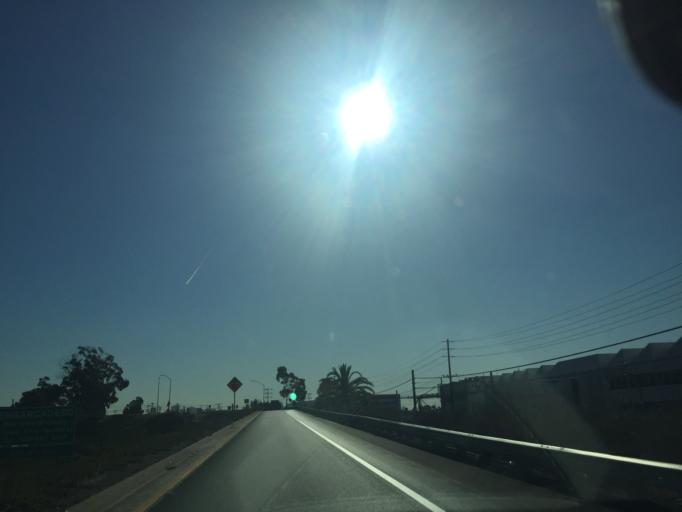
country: US
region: California
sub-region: San Diego County
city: San Diego
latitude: 32.7482
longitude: -117.1948
